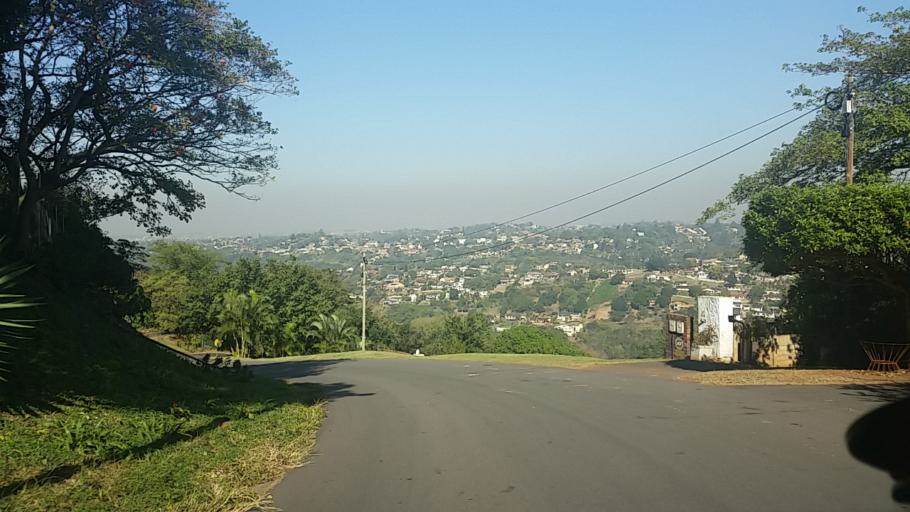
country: ZA
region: KwaZulu-Natal
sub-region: eThekwini Metropolitan Municipality
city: Berea
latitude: -29.8570
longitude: 30.9033
